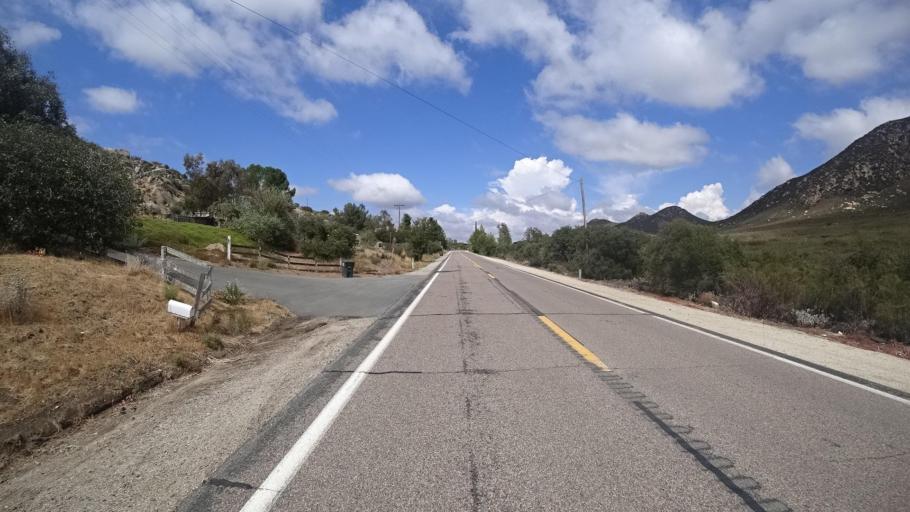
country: US
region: California
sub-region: San Diego County
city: Campo
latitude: 32.6800
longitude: -116.4888
